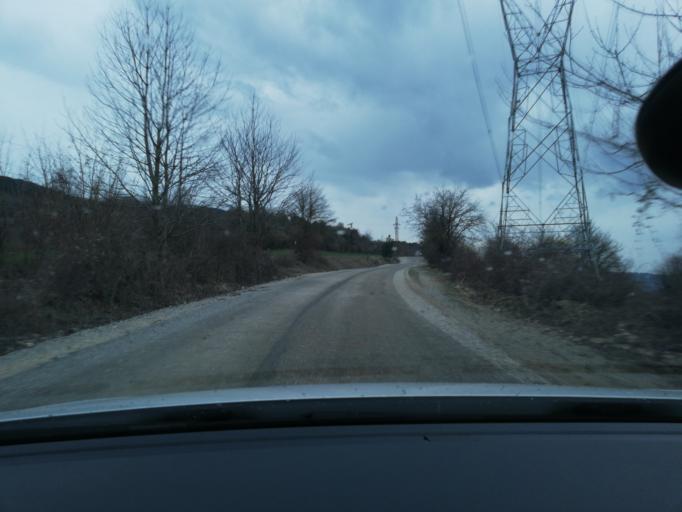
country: TR
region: Bolu
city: Gokcesu
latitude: 40.7377
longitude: 31.8372
